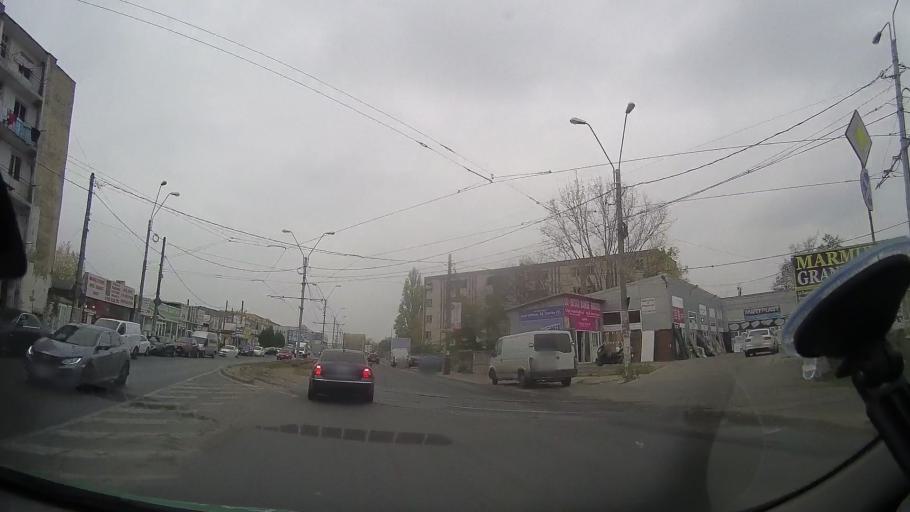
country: RO
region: Ilfov
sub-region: Comuna Chiajna
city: Rosu
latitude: 44.4291
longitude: 26.0023
